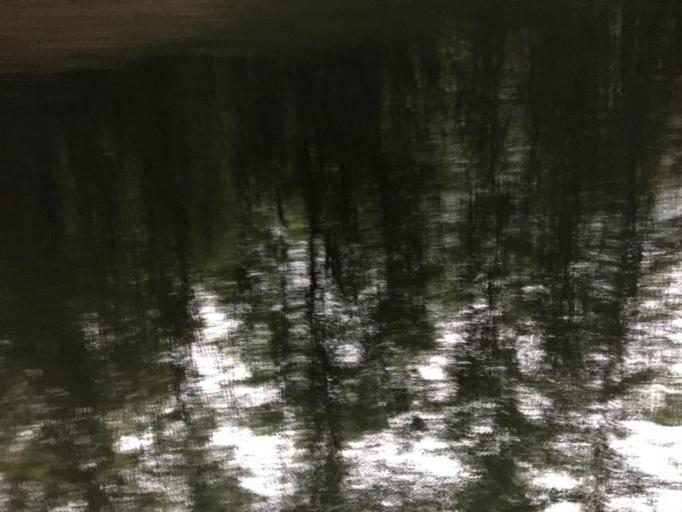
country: TW
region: Taiwan
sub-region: Chiayi
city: Jiayi Shi
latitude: 23.5140
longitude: 120.6584
